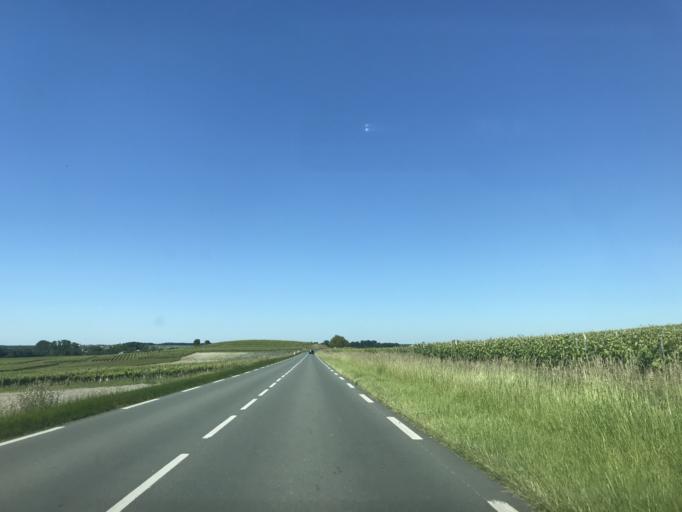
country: FR
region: Poitou-Charentes
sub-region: Departement de la Charente-Maritime
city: Perignac
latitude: 45.5767
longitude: -0.4612
